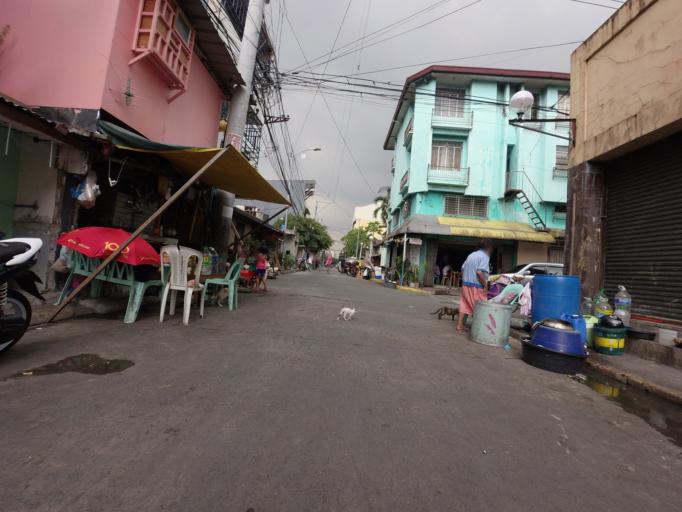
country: PH
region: Metro Manila
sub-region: City of Manila
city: Quiapo
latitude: 14.5768
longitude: 120.9955
